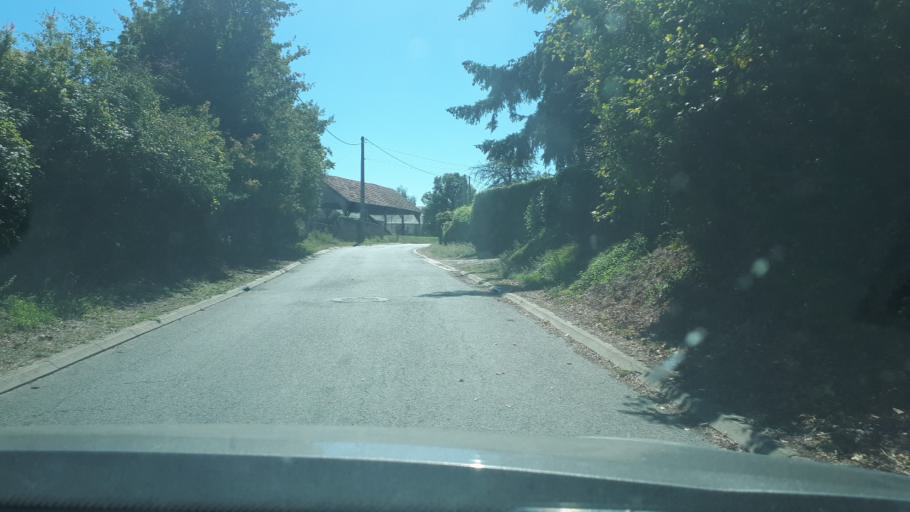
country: FR
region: Centre
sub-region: Departement du Cher
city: Baugy
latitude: 47.2091
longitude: 2.7422
